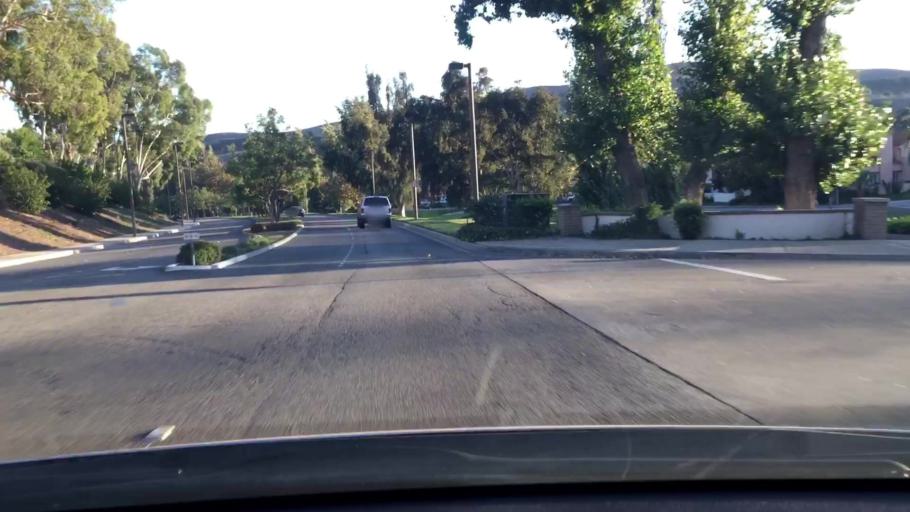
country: US
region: California
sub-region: Los Angeles County
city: Diamond Bar
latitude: 34.0322
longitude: -117.7769
